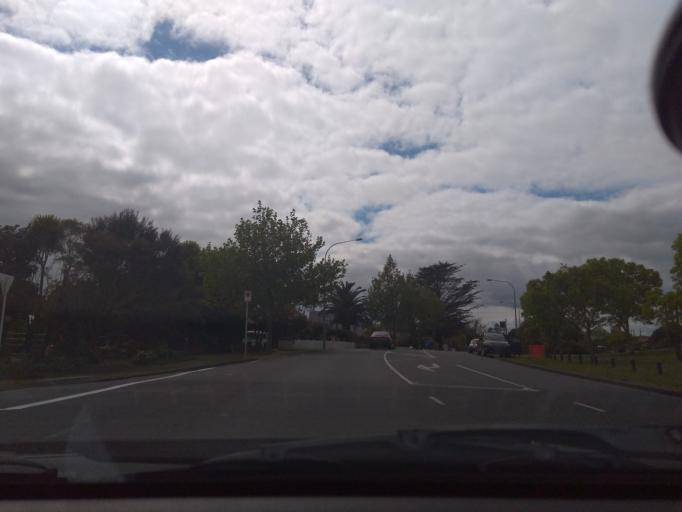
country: NZ
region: Auckland
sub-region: Auckland
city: Rosebank
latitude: -36.8655
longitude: 174.5746
